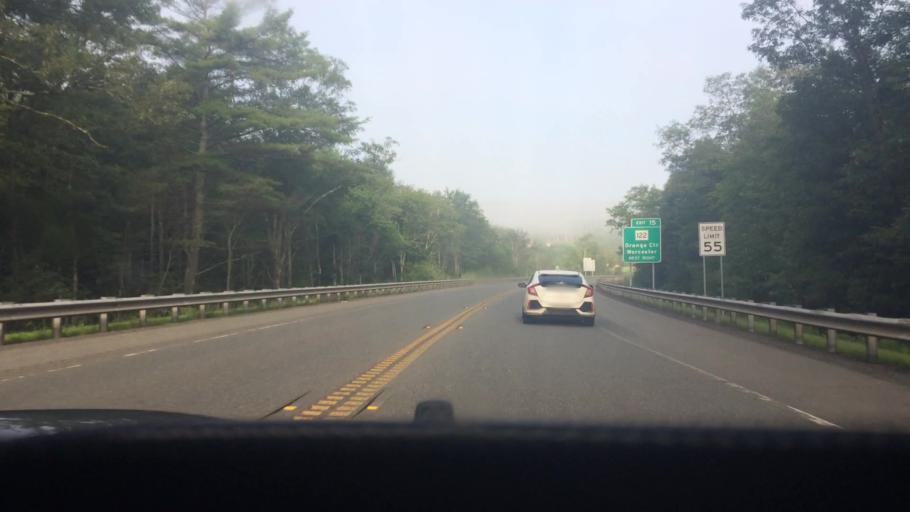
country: US
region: Massachusetts
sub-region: Franklin County
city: Orange
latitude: 42.5574
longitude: -72.2933
